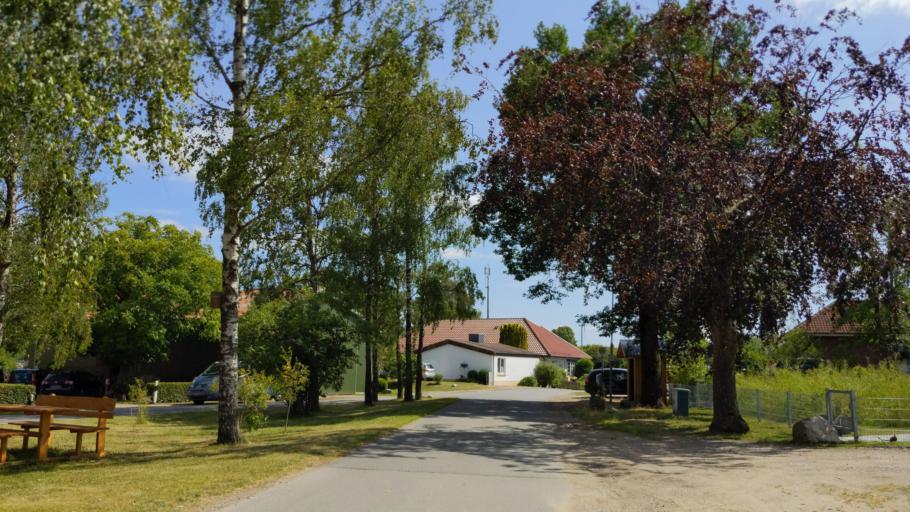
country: DE
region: Schleswig-Holstein
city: Beschendorf
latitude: 54.1654
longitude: 10.8627
